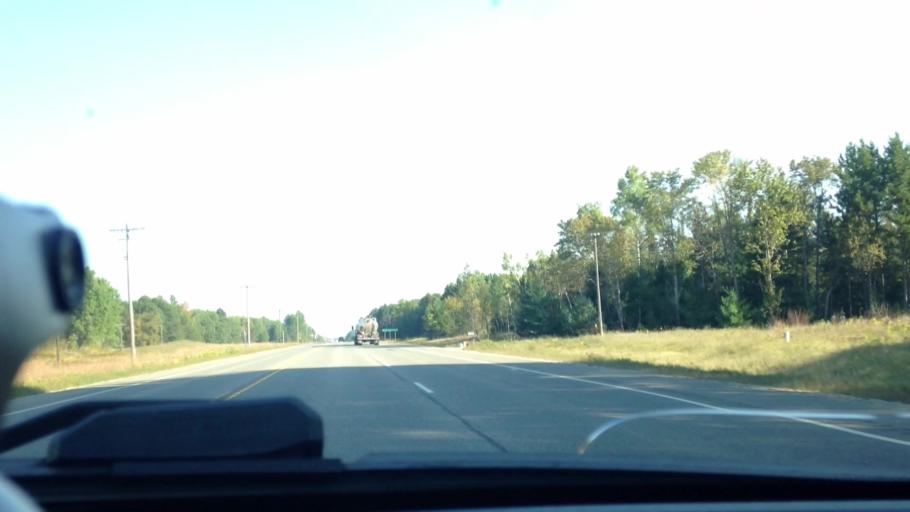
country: US
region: Wisconsin
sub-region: Marinette County
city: Niagara
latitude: 45.5384
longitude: -87.9970
